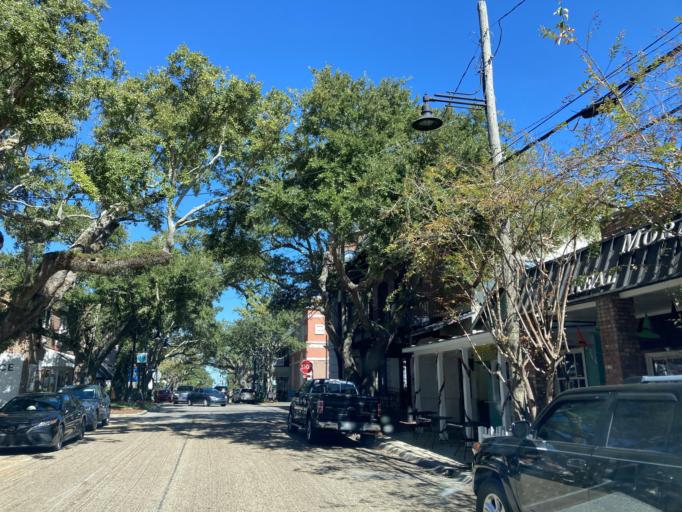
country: US
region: Mississippi
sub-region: Jackson County
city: Ocean Springs
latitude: 30.4132
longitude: -88.8278
